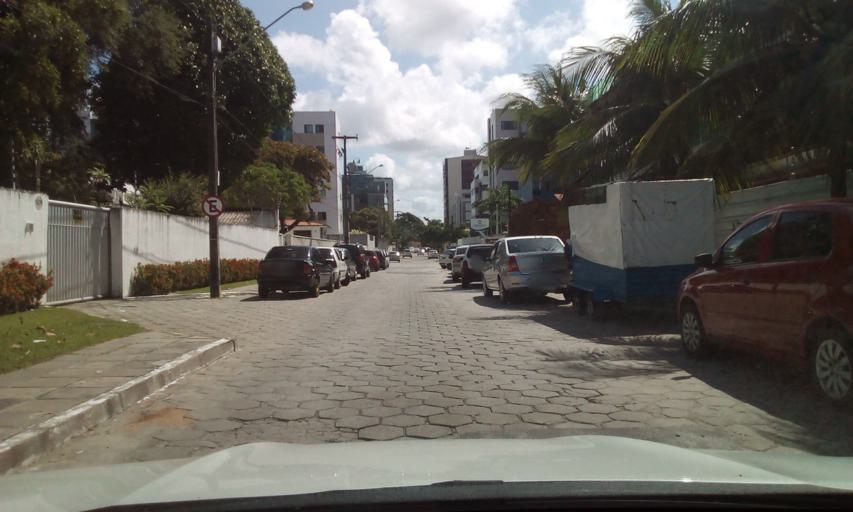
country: BR
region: Paraiba
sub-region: Joao Pessoa
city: Joao Pessoa
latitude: -7.1254
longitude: -34.8240
